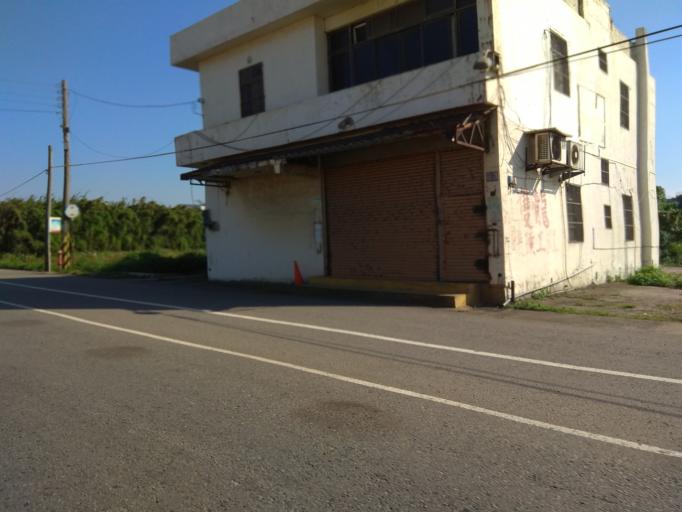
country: TW
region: Taiwan
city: Taoyuan City
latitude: 25.0343
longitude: 121.0989
